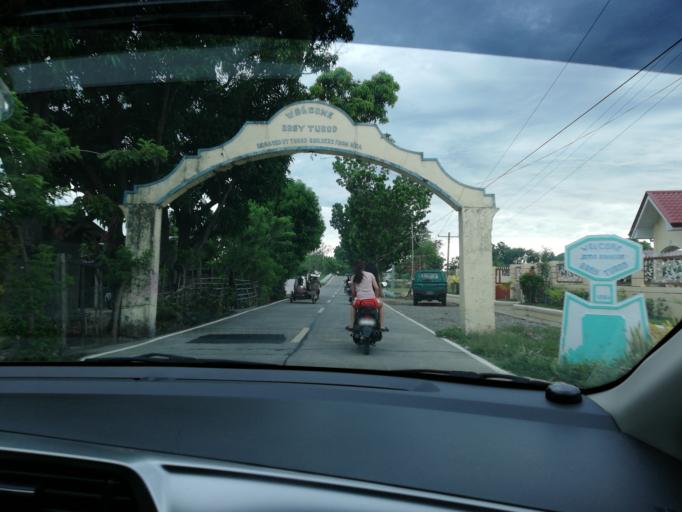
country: PH
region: Ilocos
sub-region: Province of Ilocos Sur
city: Narvacan
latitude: 17.4196
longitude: 120.4634
